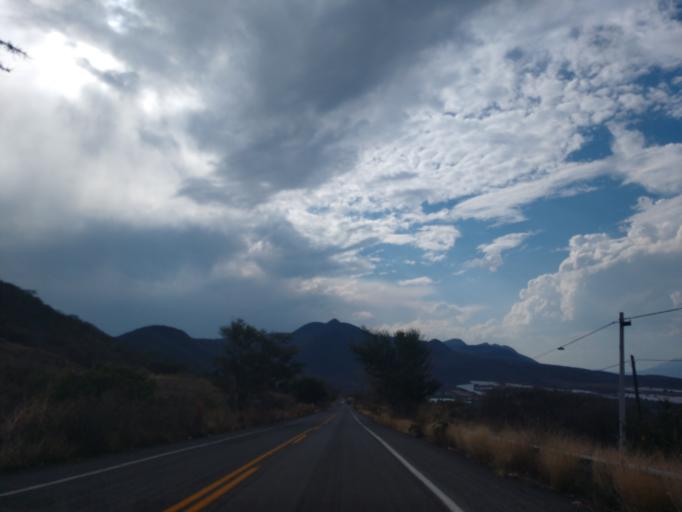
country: MX
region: Jalisco
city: La Manzanilla de la Paz
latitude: 20.1351
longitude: -103.1729
